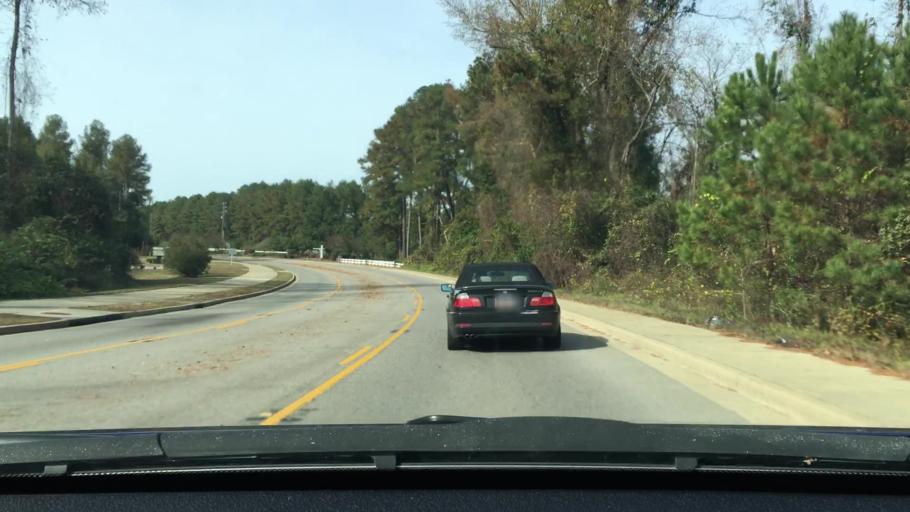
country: US
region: South Carolina
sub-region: Sumter County
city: South Sumter
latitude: 33.9184
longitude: -80.3922
